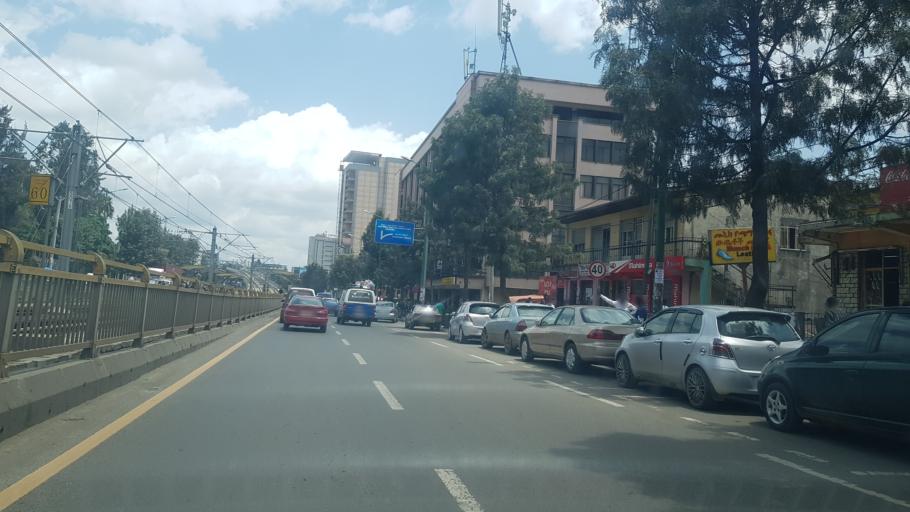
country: ET
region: Adis Abeba
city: Addis Ababa
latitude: 8.9913
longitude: 38.7590
